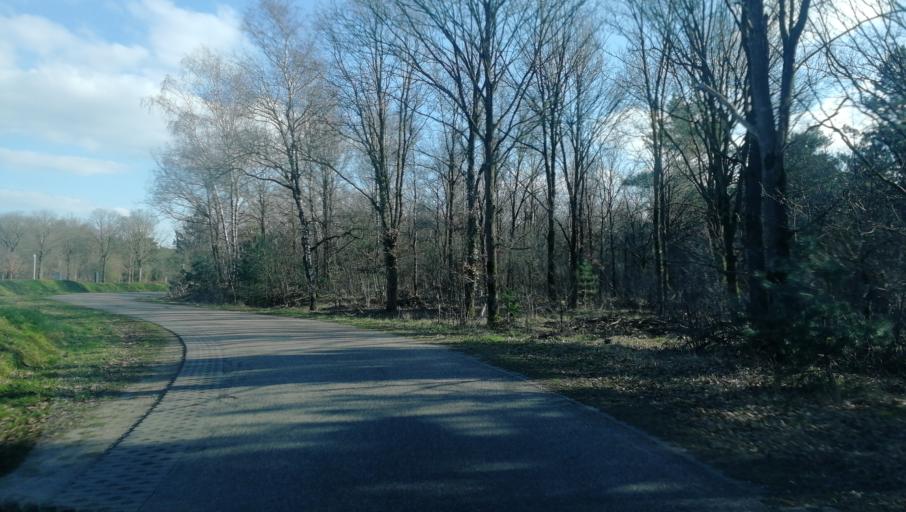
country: NL
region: Limburg
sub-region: Gemeente Peel en Maas
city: Maasbree
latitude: 51.3944
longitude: 5.9792
